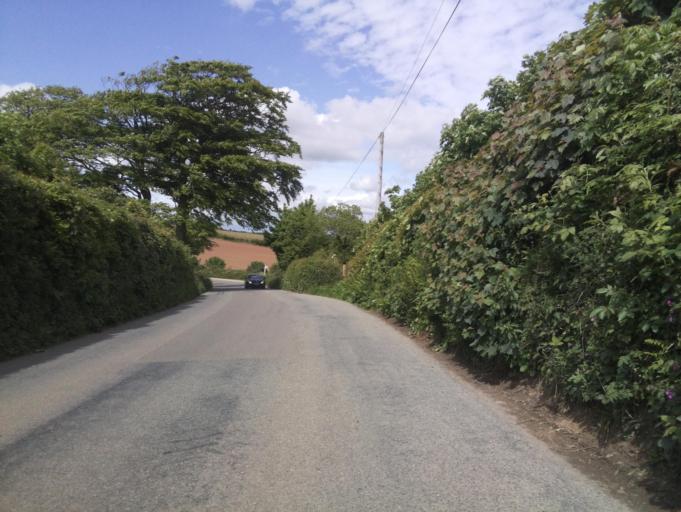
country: GB
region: England
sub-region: Devon
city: South Brent
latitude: 50.3829
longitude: -3.8315
